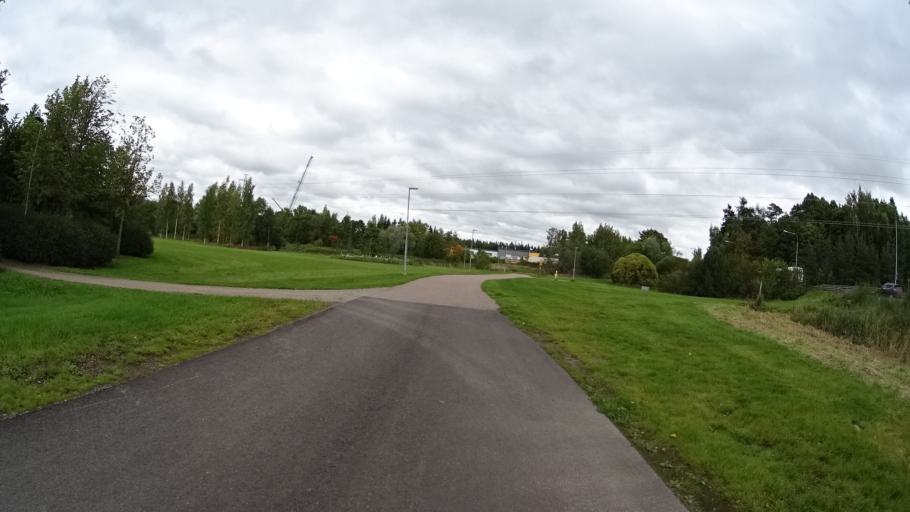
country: FI
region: Uusimaa
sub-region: Helsinki
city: Helsinki
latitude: 60.2385
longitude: 24.9762
